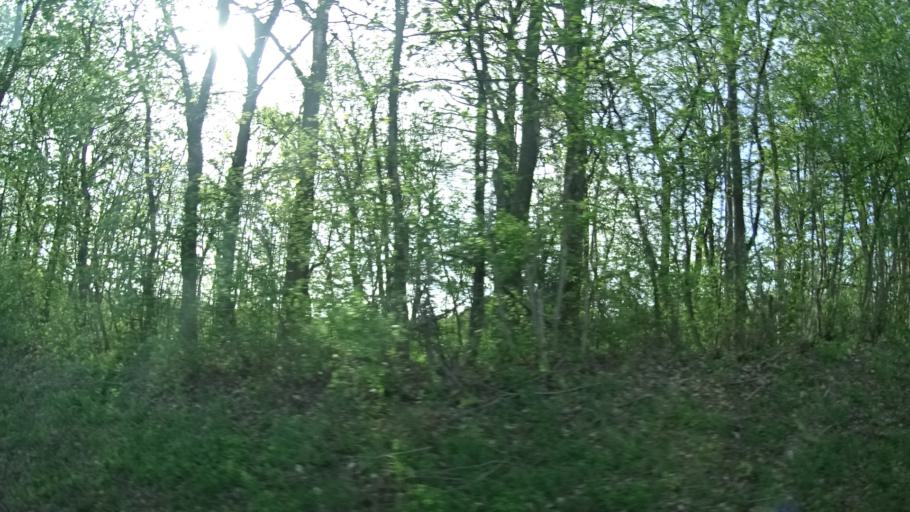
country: DE
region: Bavaria
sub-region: Regierungsbezirk Unterfranken
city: Kolitzheim
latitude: 49.8933
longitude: 10.2288
